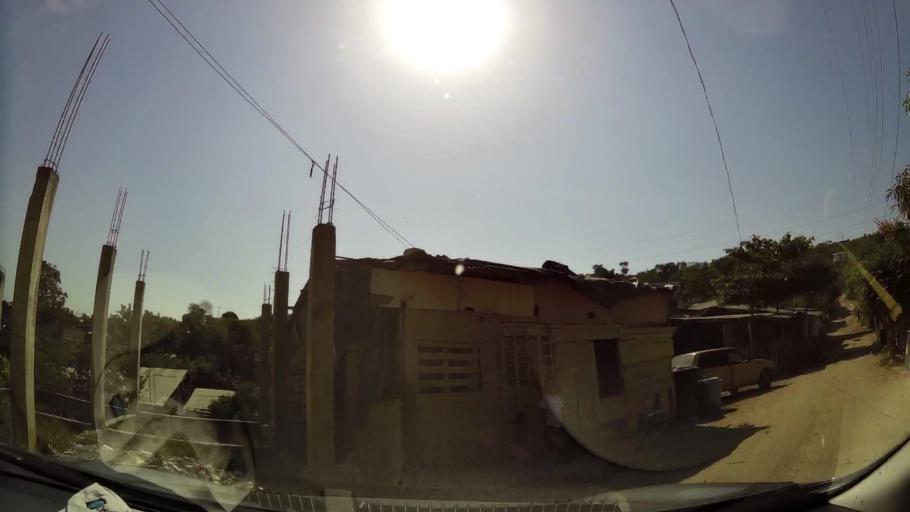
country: CO
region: Bolivar
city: Cartagena
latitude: 10.3635
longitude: -75.4992
